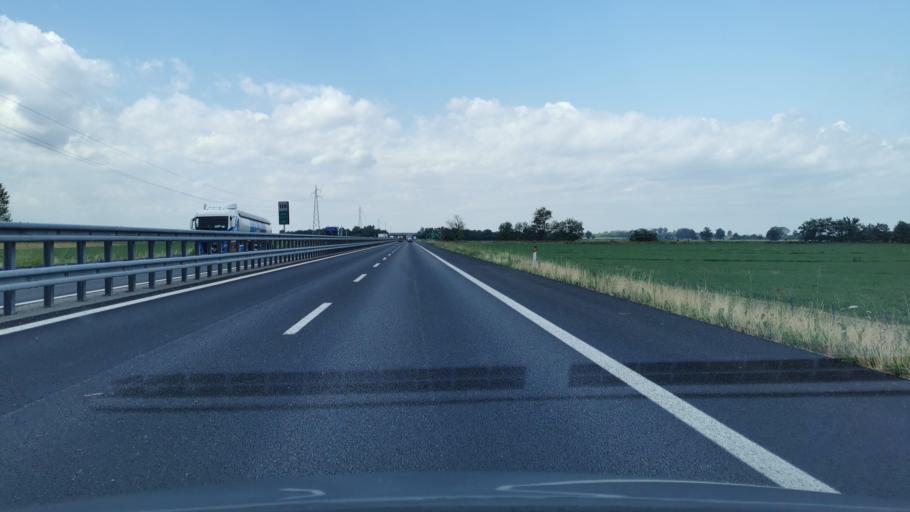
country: IT
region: Lombardy
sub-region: Provincia di Pavia
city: Redavalle
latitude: 45.0562
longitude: 9.1946
